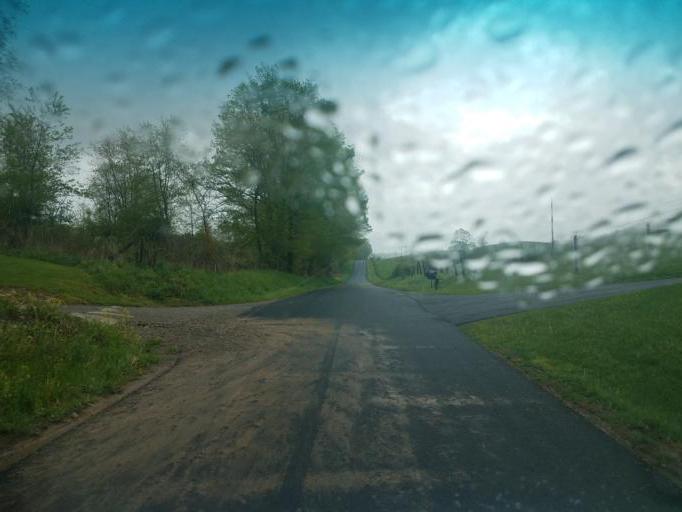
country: US
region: Virginia
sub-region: Smyth County
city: Marion
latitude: 36.9300
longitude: -81.5381
